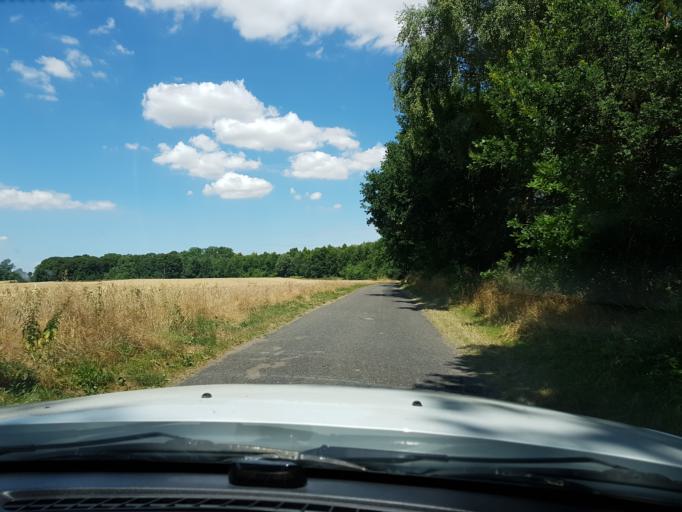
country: PL
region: West Pomeranian Voivodeship
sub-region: Powiat mysliborski
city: Barlinek
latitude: 52.9803
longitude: 15.1283
